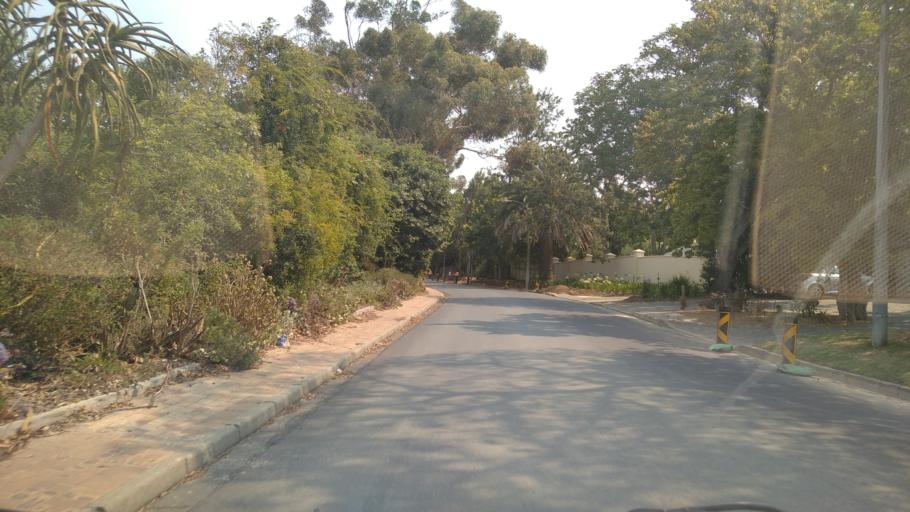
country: ZA
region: Western Cape
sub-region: City of Cape Town
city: Kraaifontein
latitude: -33.8187
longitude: 18.6582
